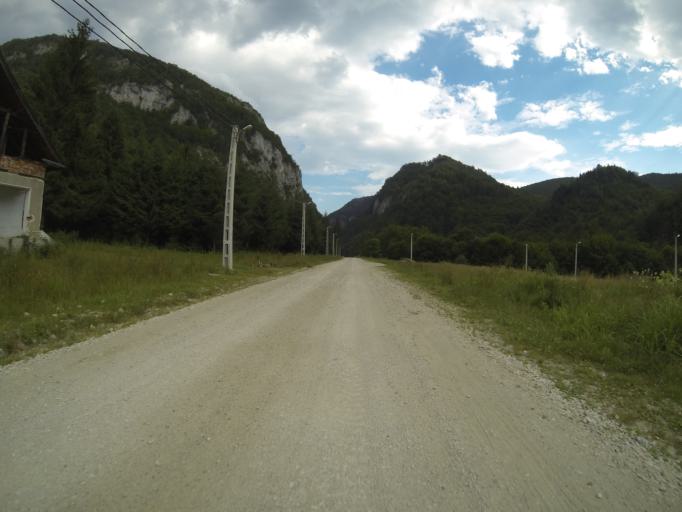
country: RO
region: Gorj
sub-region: Comuna Polovragi
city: Polovragi
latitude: 45.2149
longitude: 23.7745
